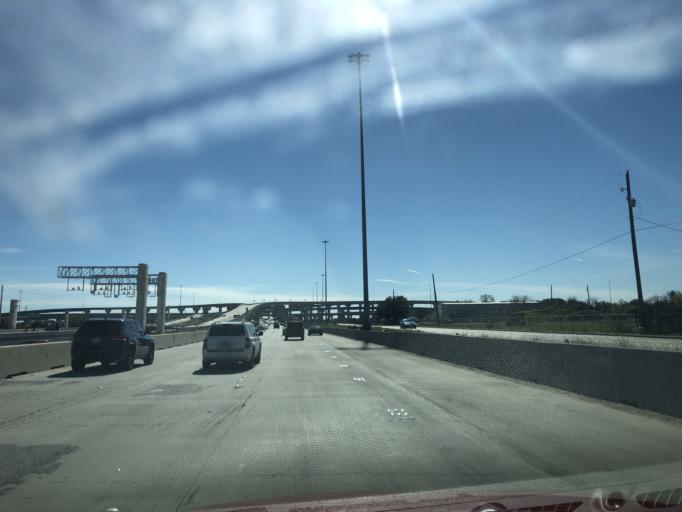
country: US
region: Texas
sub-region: Brazoria County
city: Brookside Village
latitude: 29.6050
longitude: -95.3873
